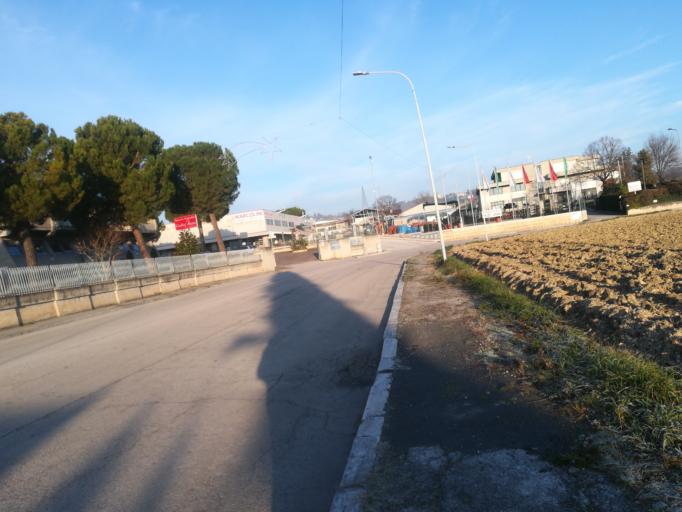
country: IT
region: The Marches
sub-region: Provincia di Macerata
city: Piediripa
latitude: 43.2784
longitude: 13.4941
